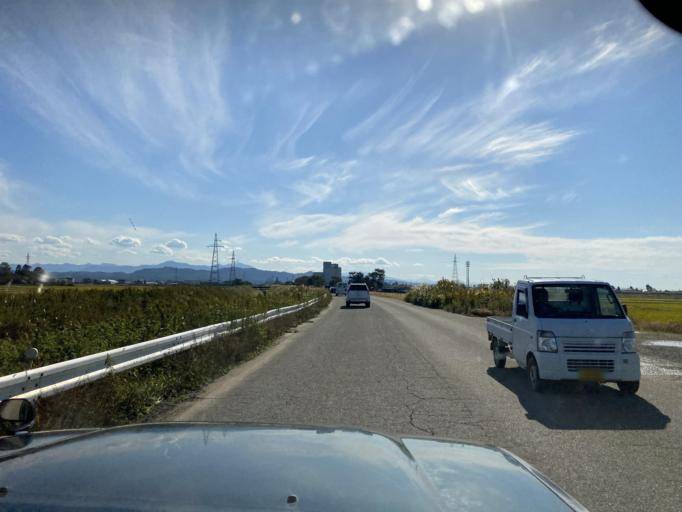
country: JP
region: Niigata
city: Niitsu-honcho
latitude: 37.7999
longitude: 139.0767
